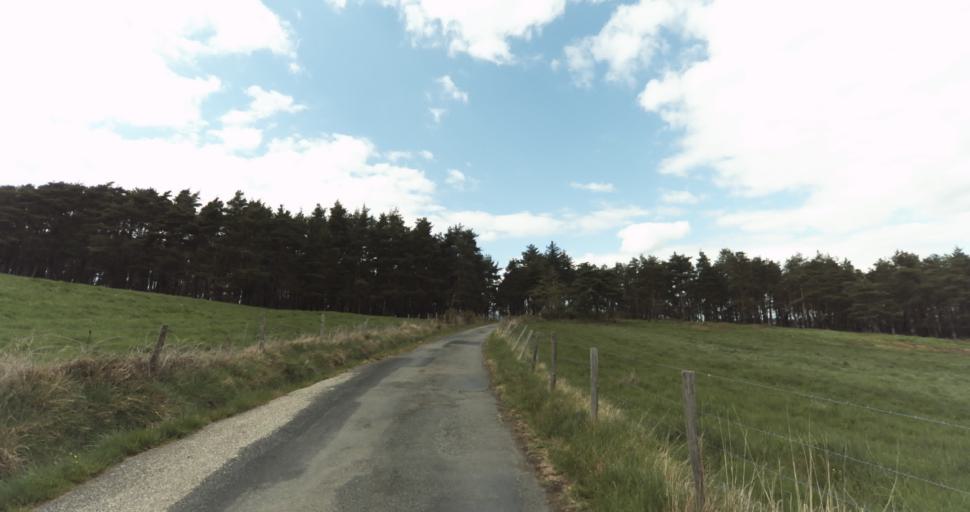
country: FR
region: Rhone-Alpes
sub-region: Departement de la Loire
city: Saint-Jean-Bonnefonds
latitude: 45.4463
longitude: 4.4612
